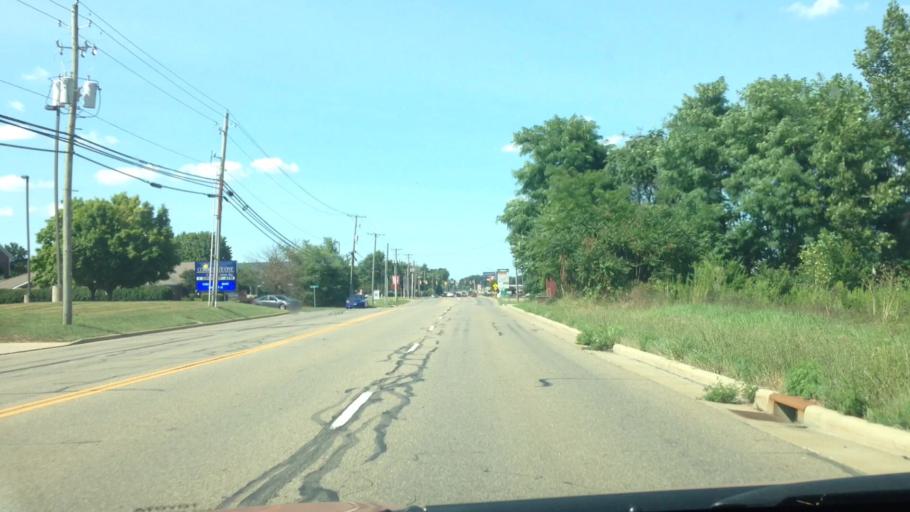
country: US
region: Ohio
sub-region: Stark County
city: North Canton
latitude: 40.8759
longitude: -81.4414
